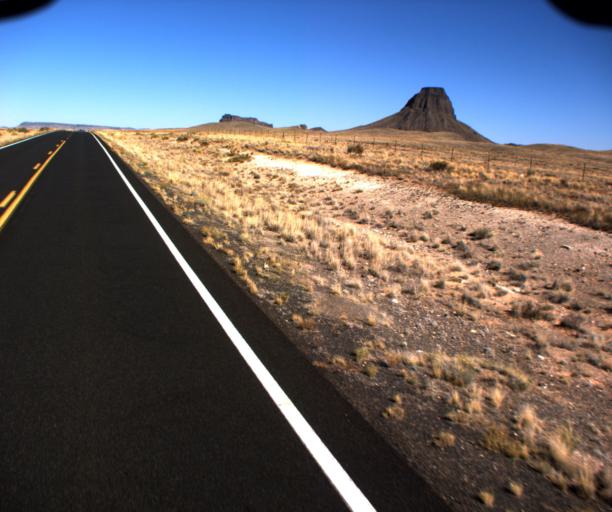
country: US
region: Arizona
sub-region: Navajo County
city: Dilkon
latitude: 35.2848
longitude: -110.4281
